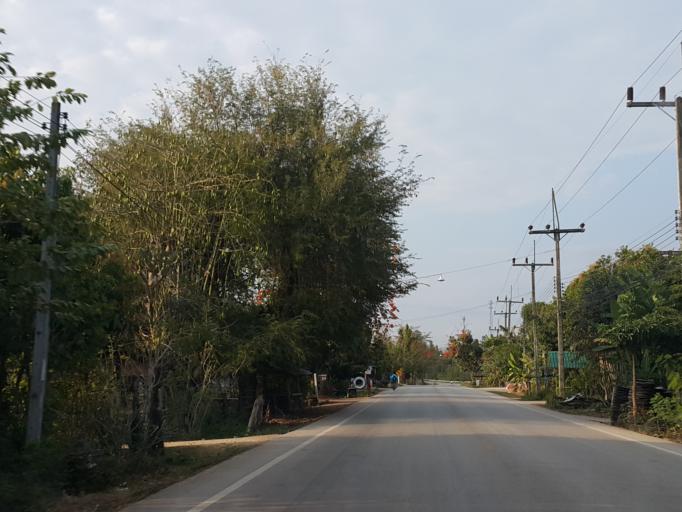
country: TH
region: Lampang
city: Chae Hom
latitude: 18.5508
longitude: 99.4766
